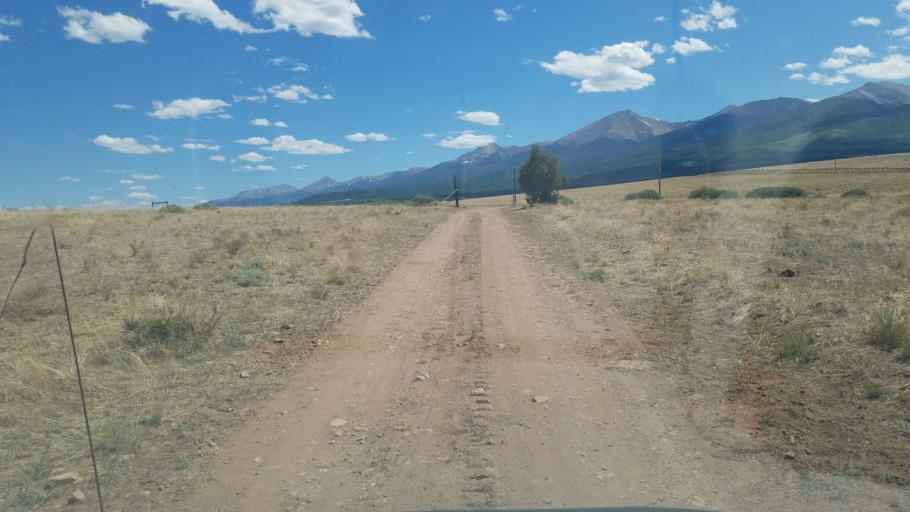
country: US
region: Colorado
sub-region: Custer County
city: Westcliffe
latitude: 38.2846
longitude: -105.6134
